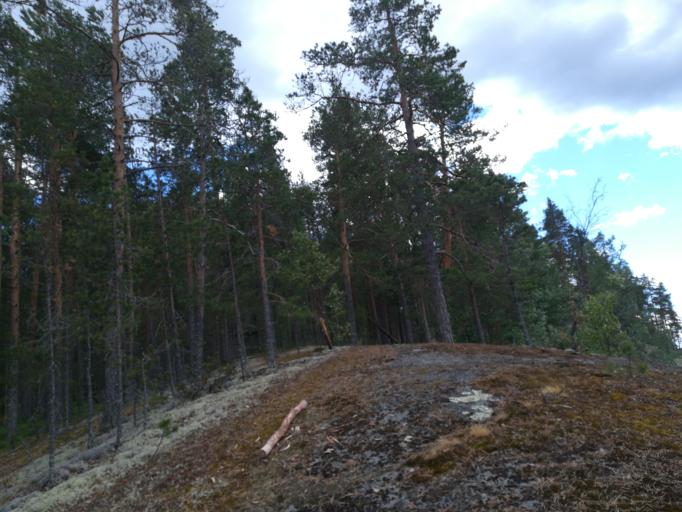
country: FI
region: Southern Savonia
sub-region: Mikkeli
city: Hirvensalmi
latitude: 61.7090
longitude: 26.9714
